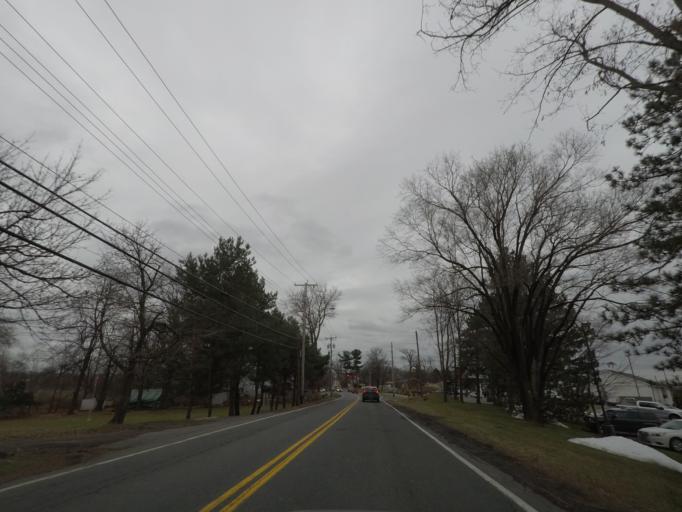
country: US
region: New York
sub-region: Albany County
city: Colonie
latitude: 42.7586
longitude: -73.7758
